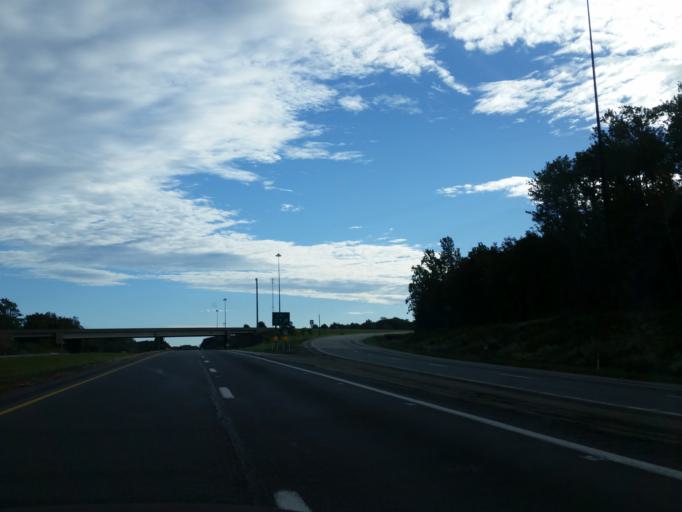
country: US
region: Pennsylvania
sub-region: Erie County
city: North East
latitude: 42.1522
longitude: -79.8952
